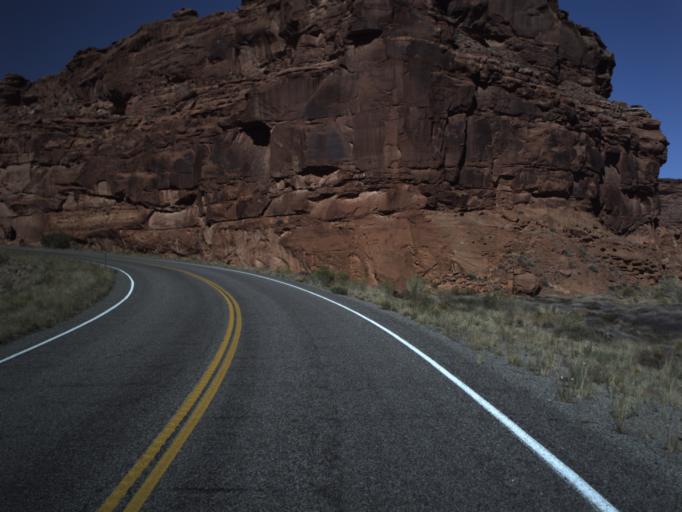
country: US
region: Utah
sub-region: San Juan County
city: Blanding
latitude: 37.9913
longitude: -110.4965
